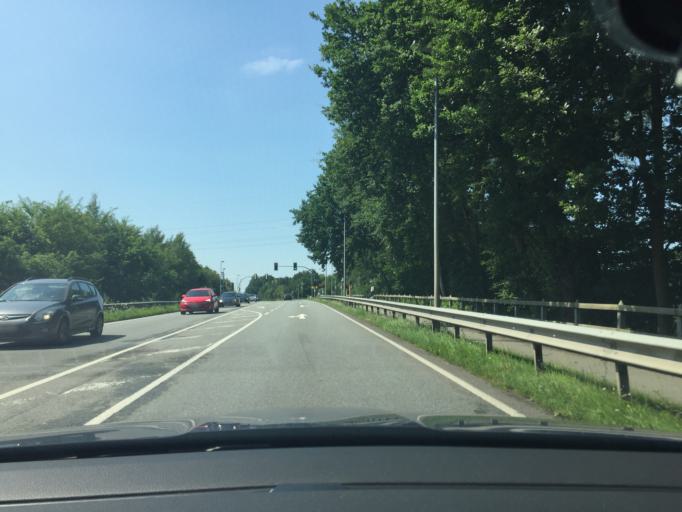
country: DE
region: Lower Saxony
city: Edewecht
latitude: 53.0983
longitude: 8.0922
